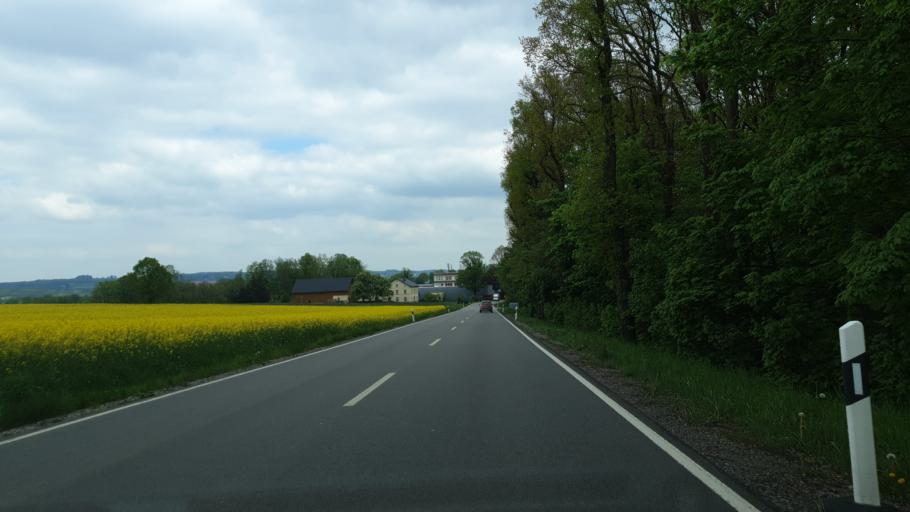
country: DE
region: Saxony
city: Bernsdorf
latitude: 50.7661
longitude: 12.6554
